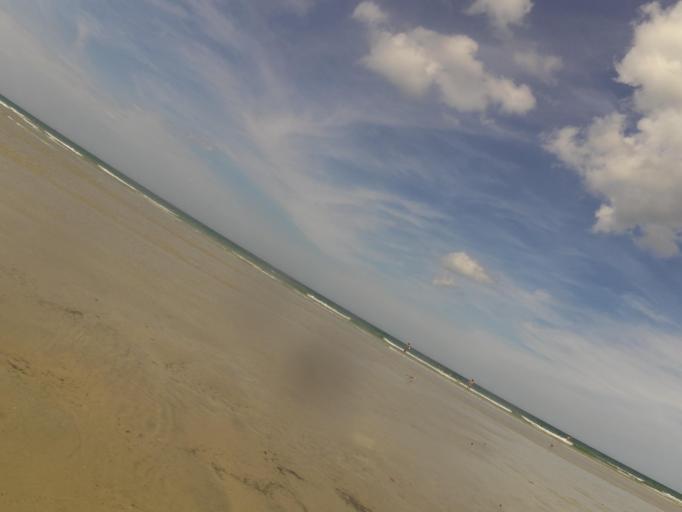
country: US
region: Florida
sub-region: Volusia County
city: Ponce Inlet
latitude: 29.0814
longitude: -80.9213
